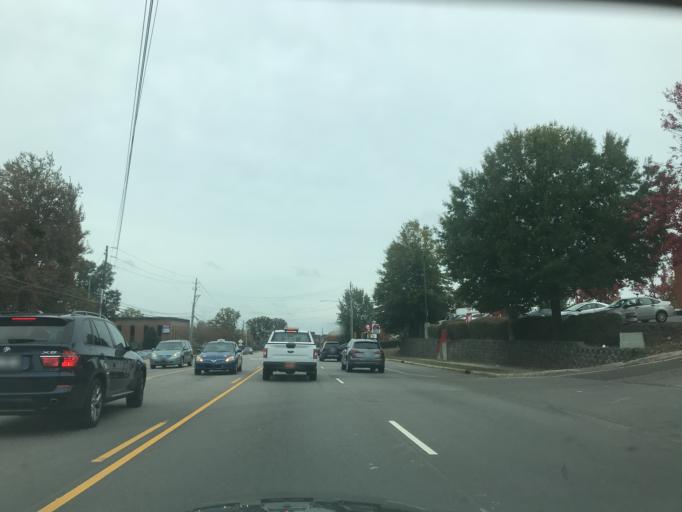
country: US
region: North Carolina
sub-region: Wake County
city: West Raleigh
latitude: 35.8713
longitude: -78.6218
